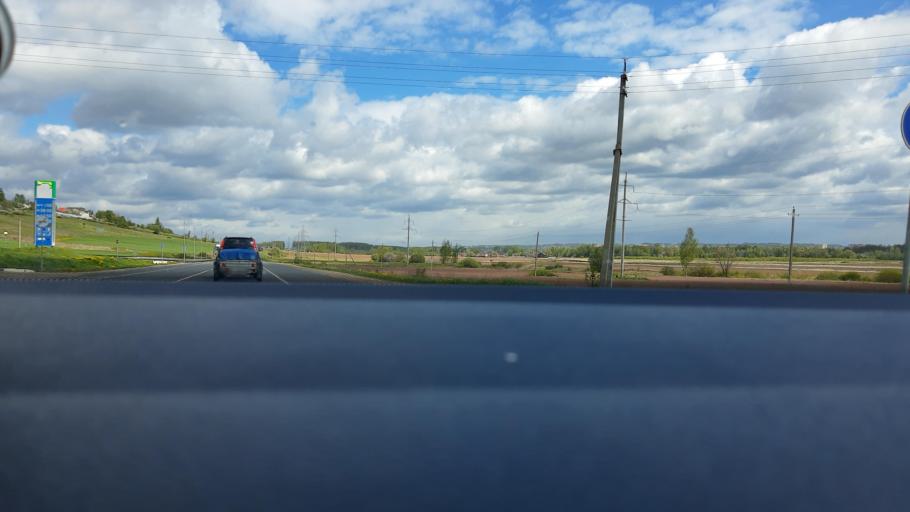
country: RU
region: Moskovskaya
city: Yakhroma
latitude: 56.3372
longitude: 37.4824
